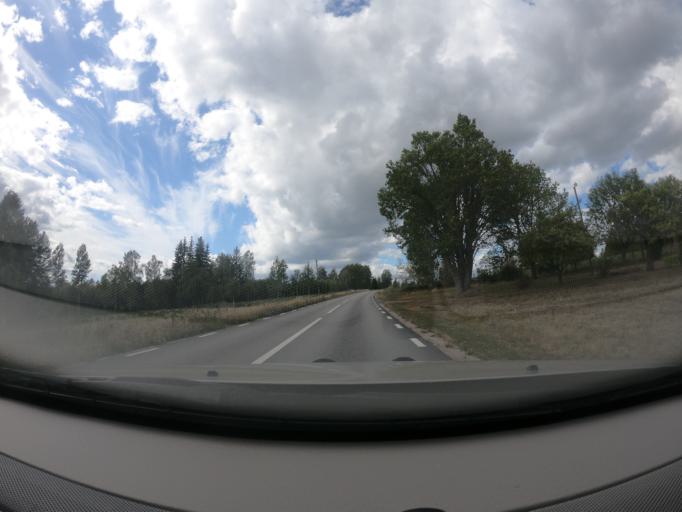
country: SE
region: Kronoberg
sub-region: Vaxjo Kommun
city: Braas
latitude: 57.1383
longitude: 14.9663
